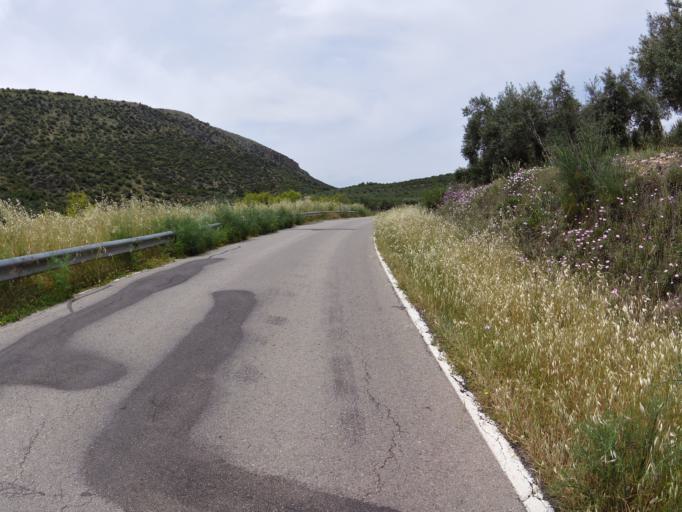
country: ES
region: Andalusia
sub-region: Province of Cordoba
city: Luque
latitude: 37.5188
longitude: -4.2217
